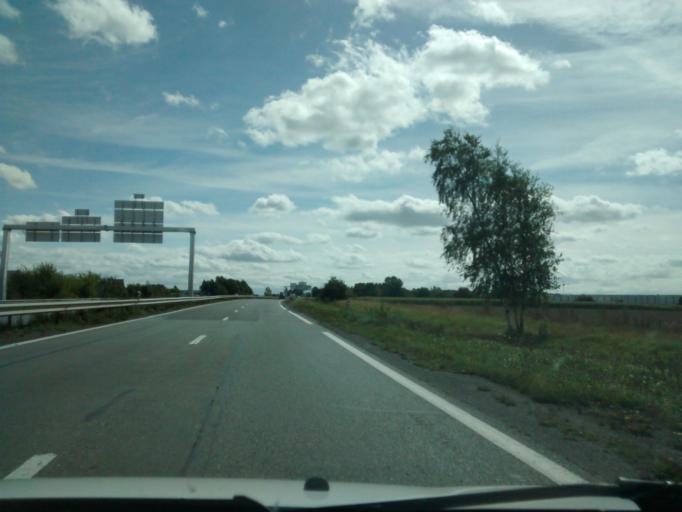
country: FR
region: Brittany
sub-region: Departement d'Ille-et-Vilaine
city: Miniac-Morvan
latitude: 48.5395
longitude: -1.9199
